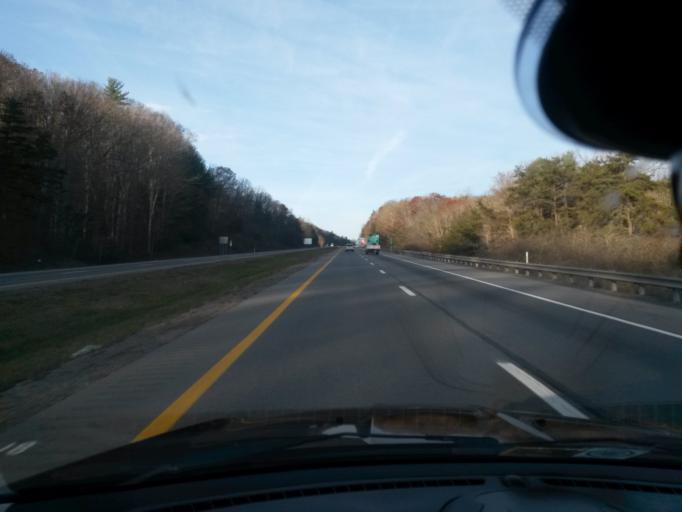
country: US
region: West Virginia
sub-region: Greenbrier County
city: Lewisburg
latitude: 37.8071
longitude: -80.4005
